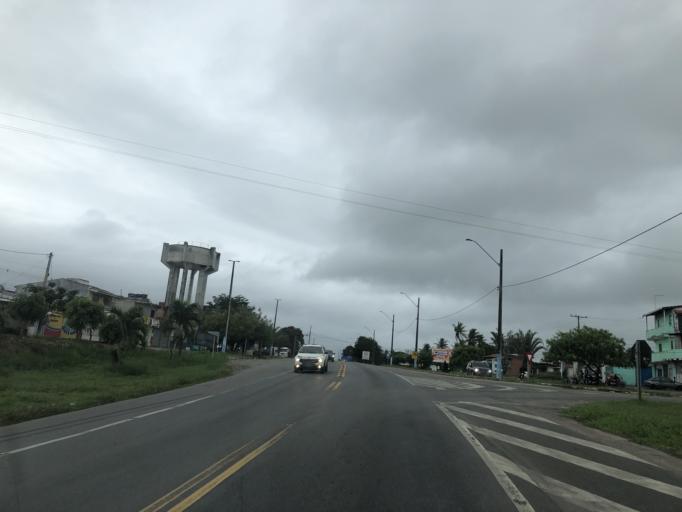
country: BR
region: Bahia
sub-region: Cruz Das Almas
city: Cruz das Almas
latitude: -12.6011
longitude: -39.0499
